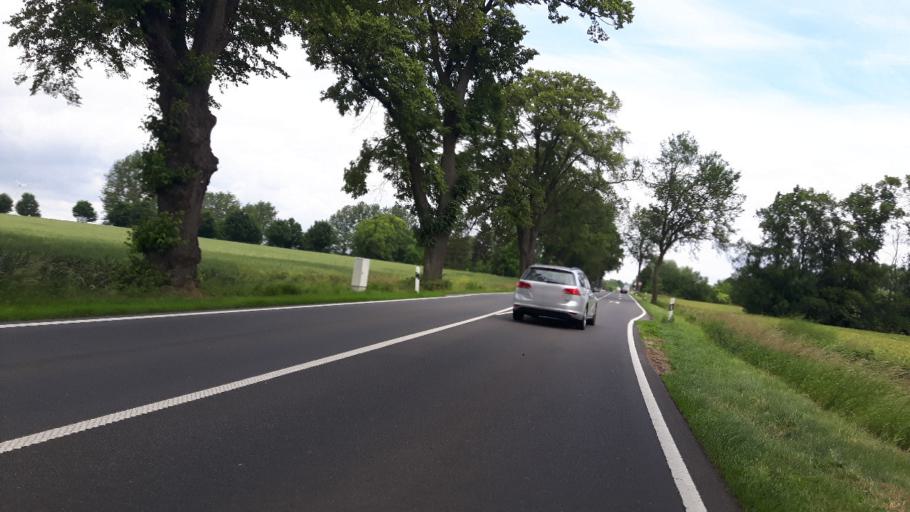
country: PL
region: West Pomeranian Voivodeship
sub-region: Powiat policki
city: Kolbaskowo
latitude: 53.3042
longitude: 14.4078
